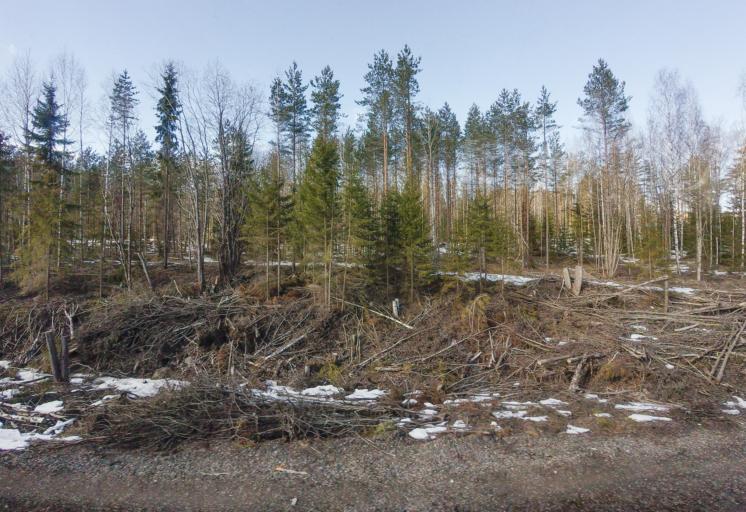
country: FI
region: South Karelia
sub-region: Lappeenranta
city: Lappeenranta
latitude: 61.0221
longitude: 28.1514
